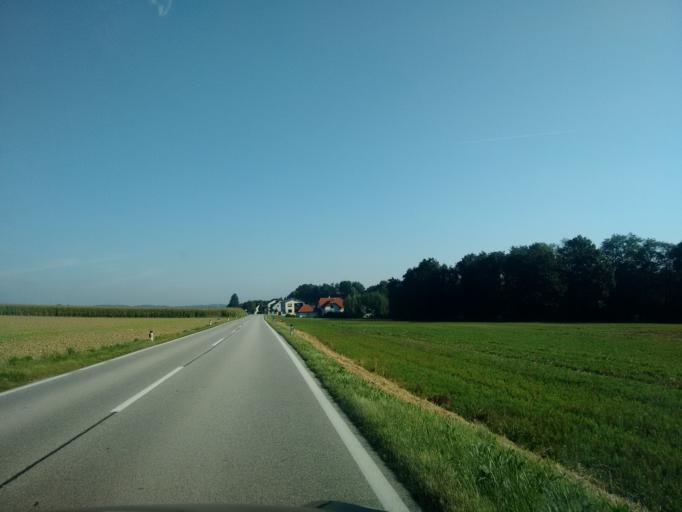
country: AT
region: Upper Austria
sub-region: Politischer Bezirk Steyr-Land
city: Bad Hall
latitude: 48.0827
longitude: 14.1921
